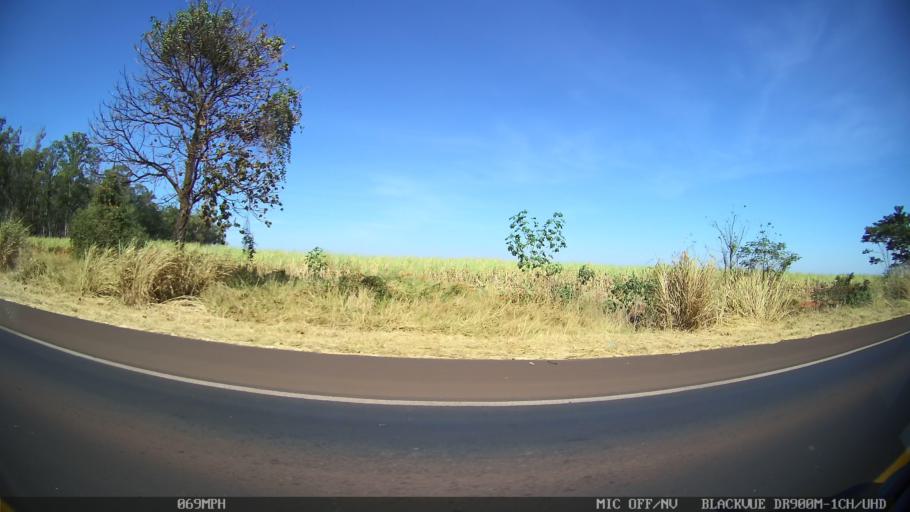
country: BR
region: Sao Paulo
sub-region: Barretos
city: Barretos
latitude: -20.4947
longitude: -48.5297
